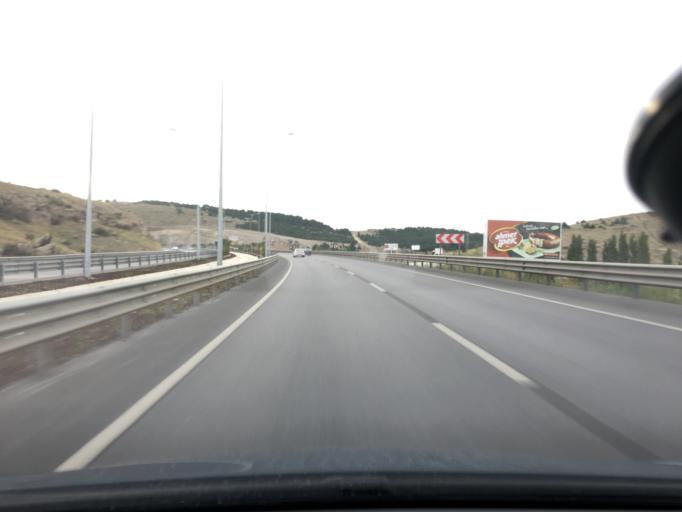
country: TR
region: Afyonkarahisar
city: Afyonkarahisar
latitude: 38.7946
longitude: 30.4426
